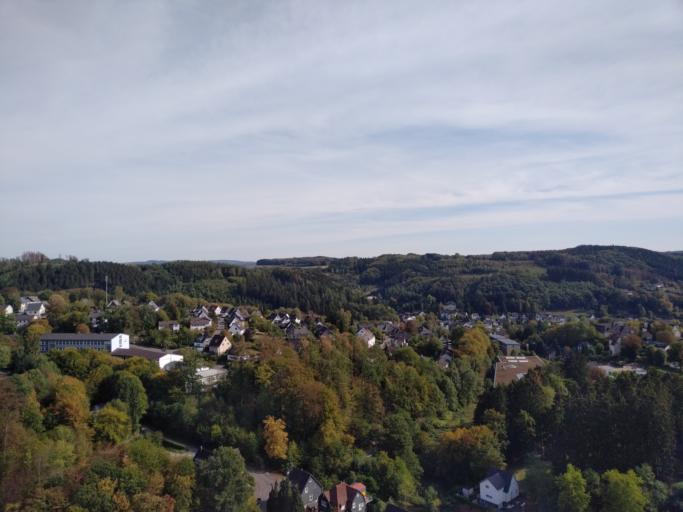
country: DE
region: North Rhine-Westphalia
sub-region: Regierungsbezirk Koln
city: Gummersbach
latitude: 51.0299
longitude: 7.5702
